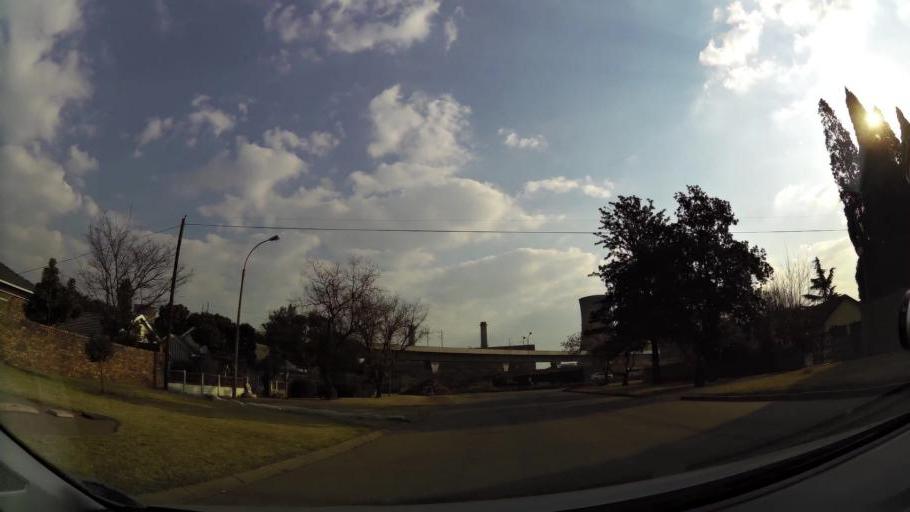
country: ZA
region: Gauteng
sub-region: City of Johannesburg Metropolitan Municipality
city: Modderfontein
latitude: -26.1127
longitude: 28.1993
